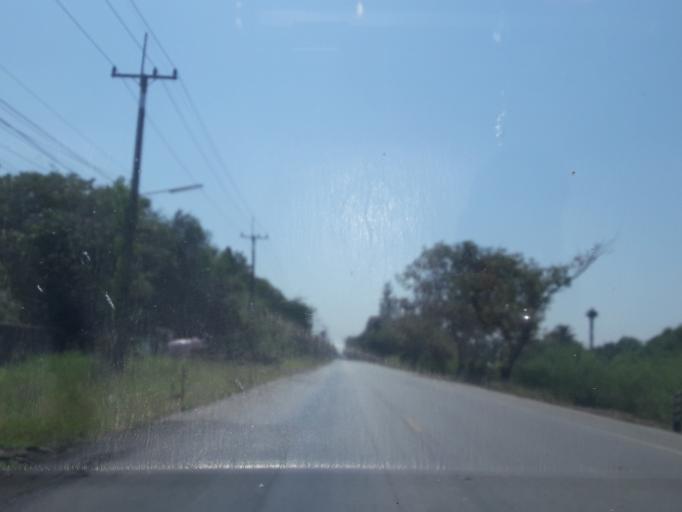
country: TH
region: Pathum Thani
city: Nong Suea
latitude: 14.1615
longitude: 100.8237
